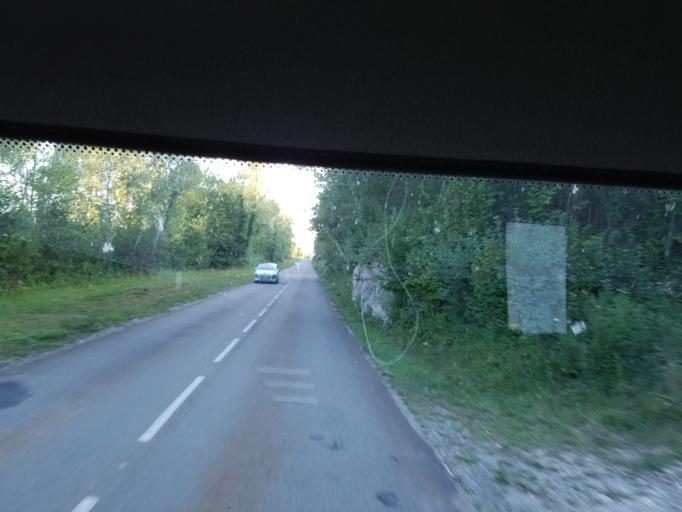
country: FR
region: Franche-Comte
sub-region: Departement du Jura
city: Moirans-en-Montagne
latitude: 46.4021
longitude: 5.6673
